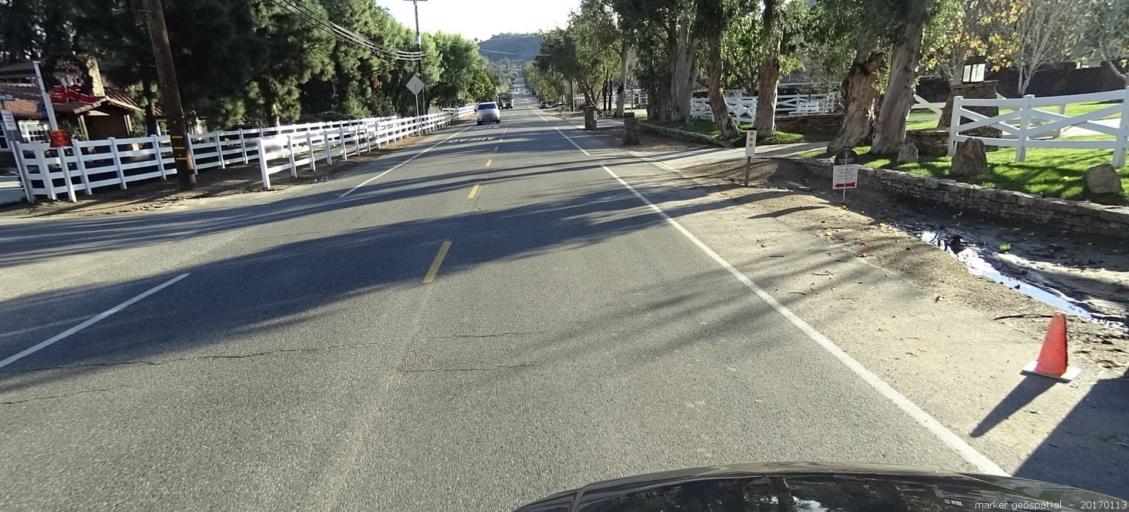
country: US
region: California
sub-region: Orange County
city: Villa Park
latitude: 33.8041
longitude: -117.7825
